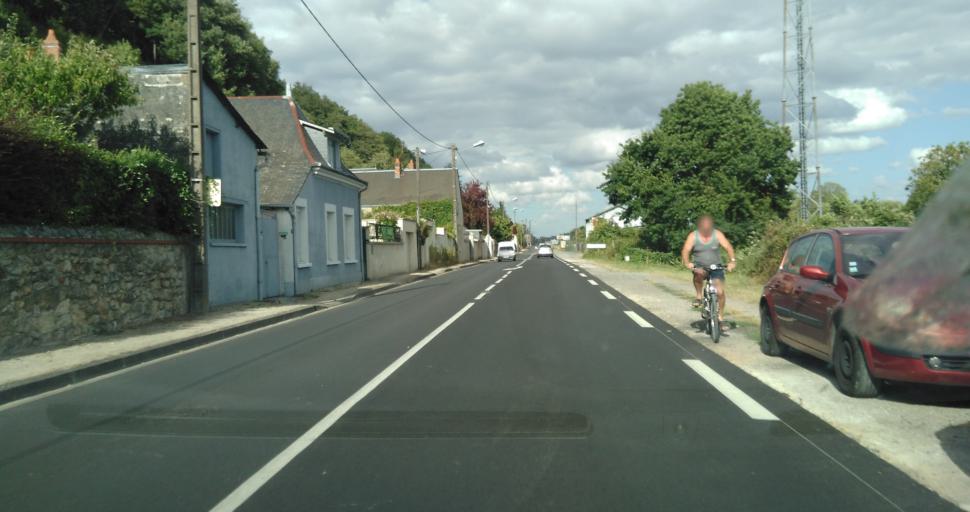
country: FR
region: Centre
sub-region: Departement d'Indre-et-Loire
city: Langeais
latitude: 47.3191
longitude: 0.3944
